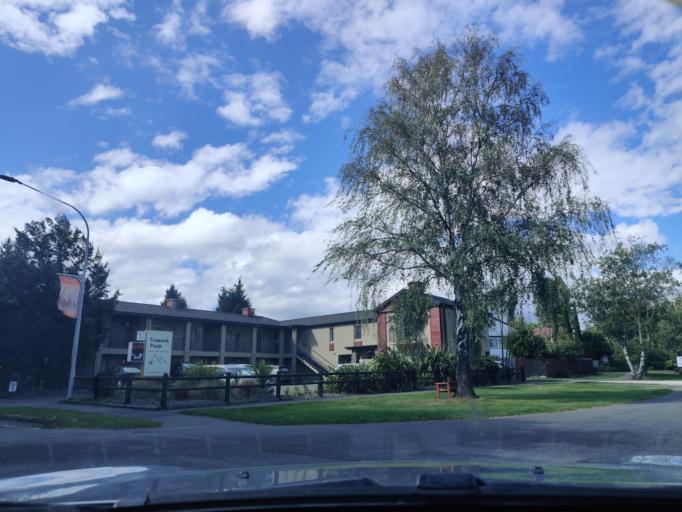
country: NZ
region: Canterbury
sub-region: Hurunui District
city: Amberley
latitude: -42.5255
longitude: 172.8291
